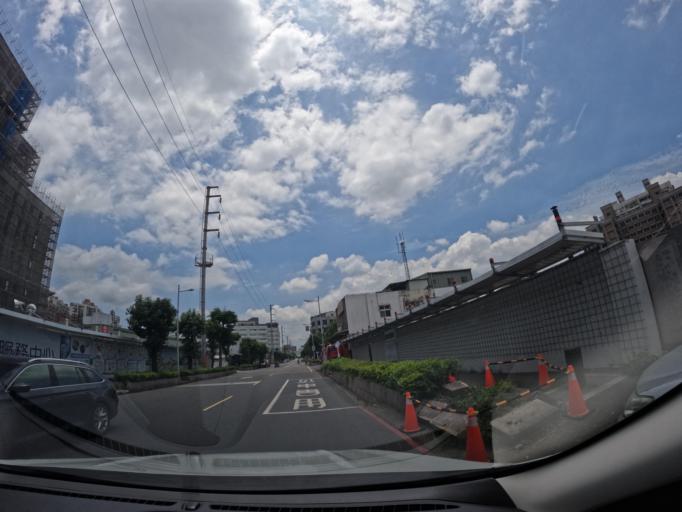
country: TW
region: Taipei
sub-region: Taipei
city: Banqiao
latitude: 24.9631
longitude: 121.4218
